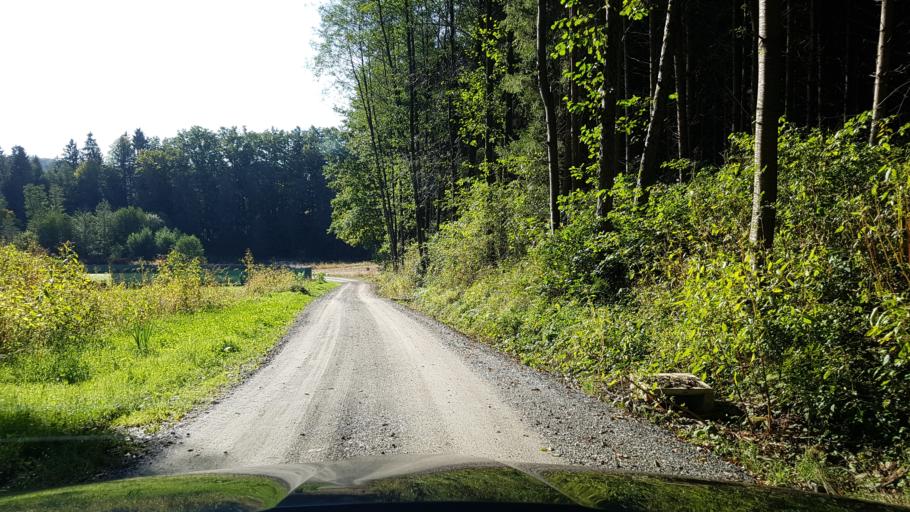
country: AT
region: Styria
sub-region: Politischer Bezirk Deutschlandsberg
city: Sankt Martin im Sulmtal
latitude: 46.7400
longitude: 15.3168
